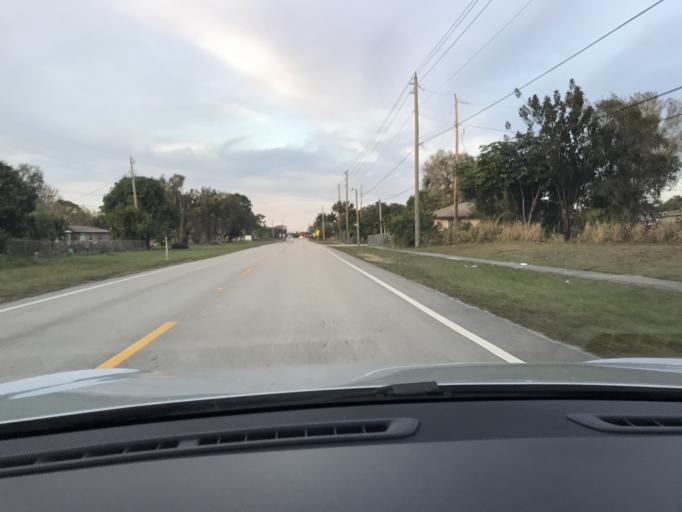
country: US
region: Florida
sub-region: Indian River County
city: Gifford
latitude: 27.6773
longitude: -80.4296
